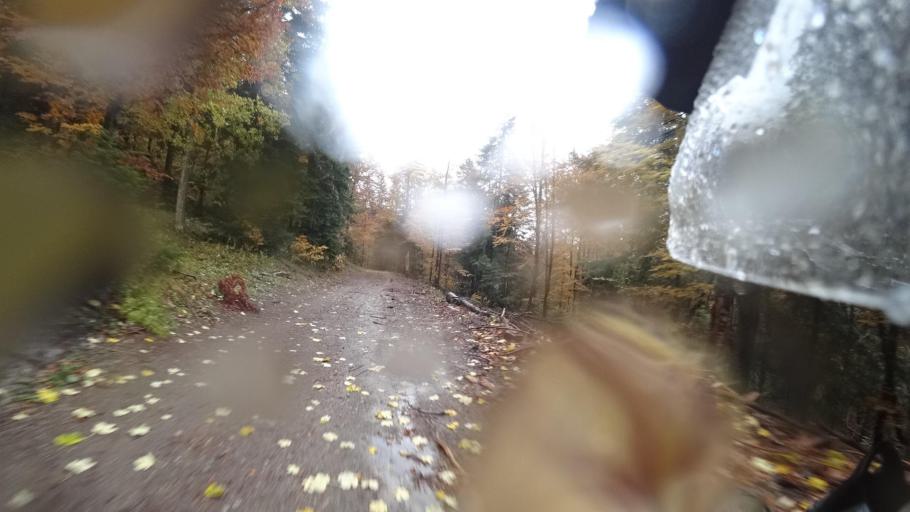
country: HR
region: Primorsko-Goranska
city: Vrbovsko
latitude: 45.2934
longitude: 15.0418
